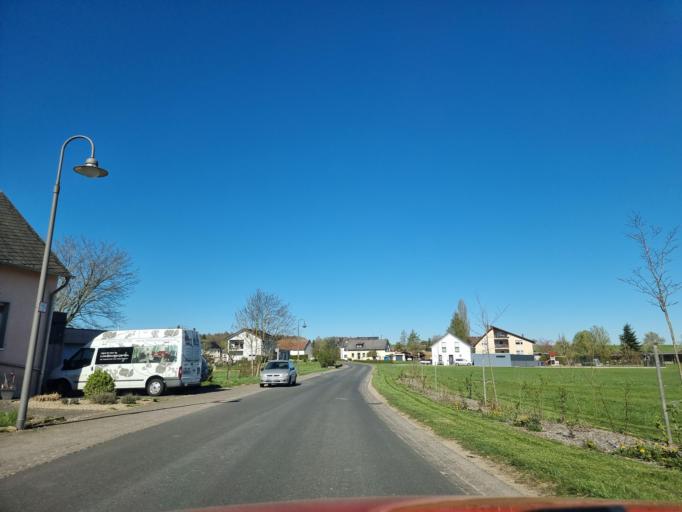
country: DE
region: Rheinland-Pfalz
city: Idenheim
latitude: 49.8985
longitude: 6.5673
